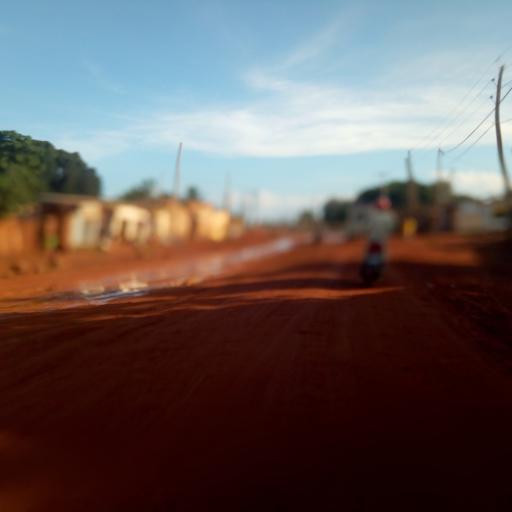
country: BJ
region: Atlantique
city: Hevie
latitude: 6.4160
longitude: 2.2632
